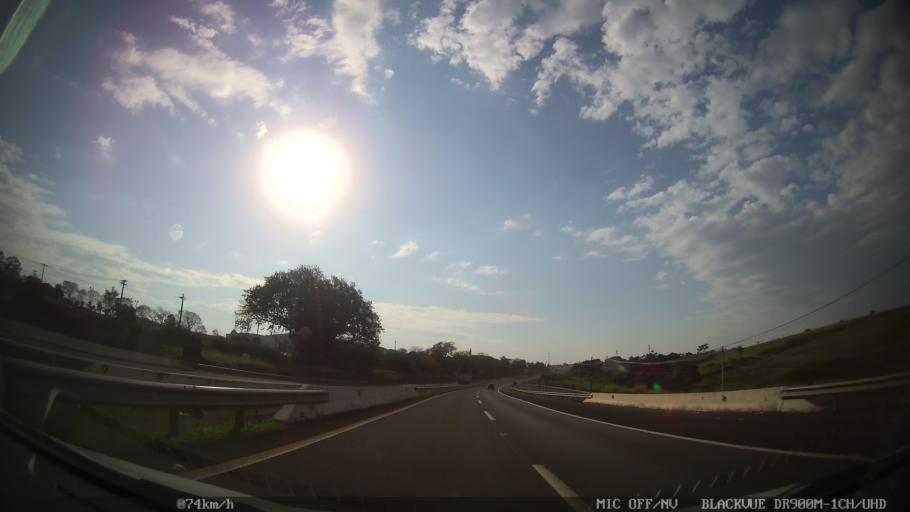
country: BR
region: Sao Paulo
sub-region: Cosmopolis
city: Cosmopolis
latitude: -22.6841
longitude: -47.1584
